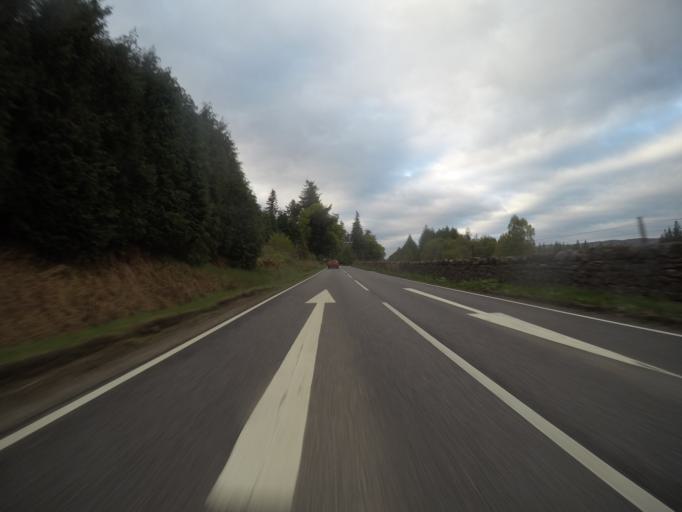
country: GB
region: Scotland
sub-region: Highland
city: Spean Bridge
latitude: 57.1068
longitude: -4.7191
